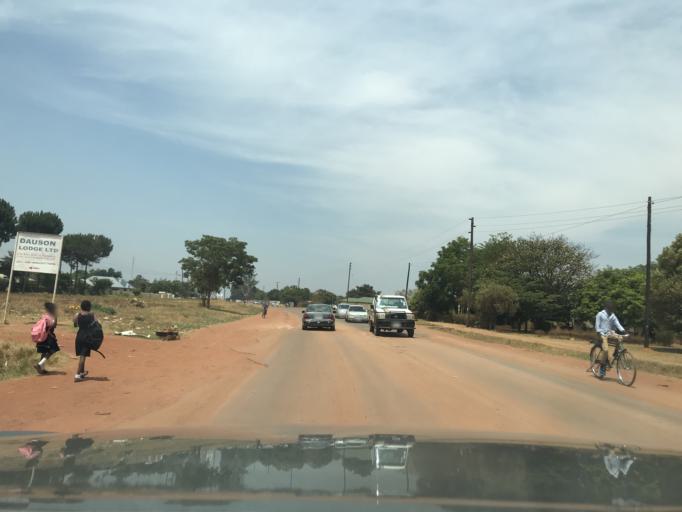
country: ZM
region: Northern
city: Kasama
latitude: -10.2051
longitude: 31.1806
